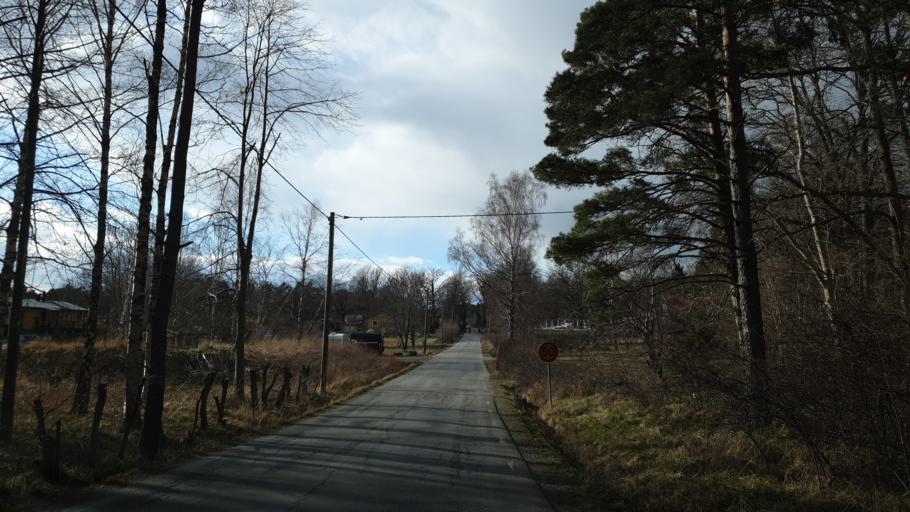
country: SE
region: Stockholm
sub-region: Varmdo Kommun
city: Holo
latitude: 59.3588
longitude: 18.6567
